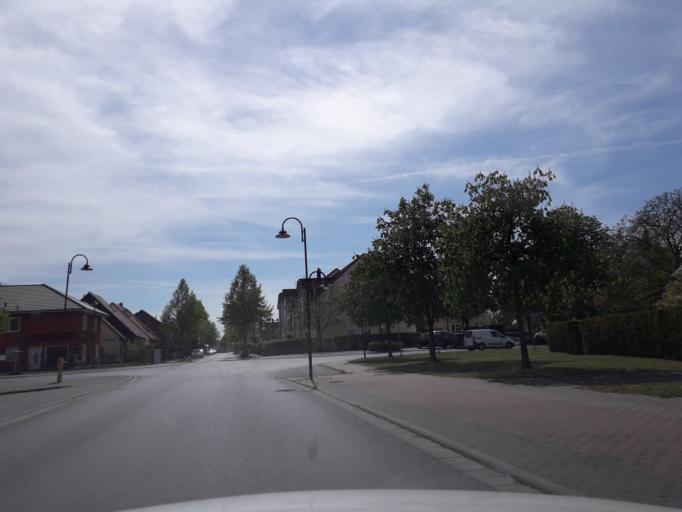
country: DE
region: Brandenburg
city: Wustermark
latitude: 52.5465
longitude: 12.9378
